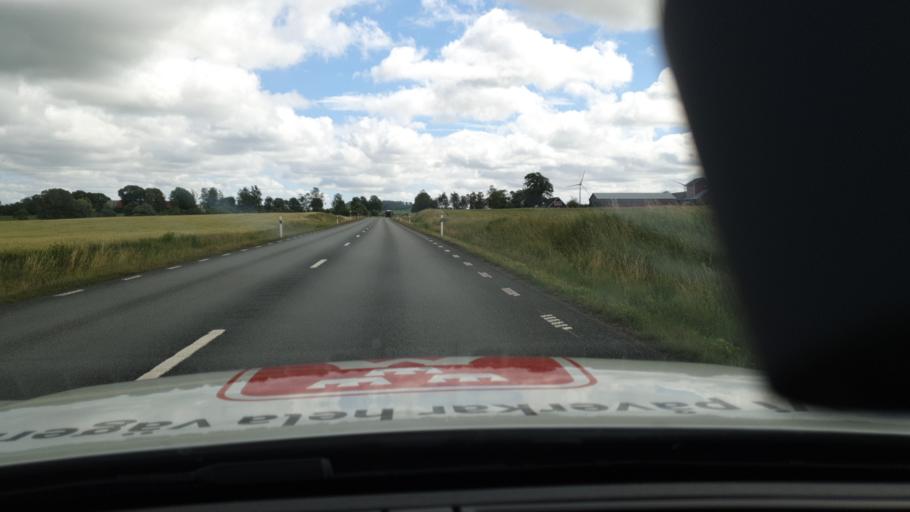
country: SE
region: Vaestra Goetaland
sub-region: Falkopings Kommun
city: Akarp
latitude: 58.1248
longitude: 13.7122
